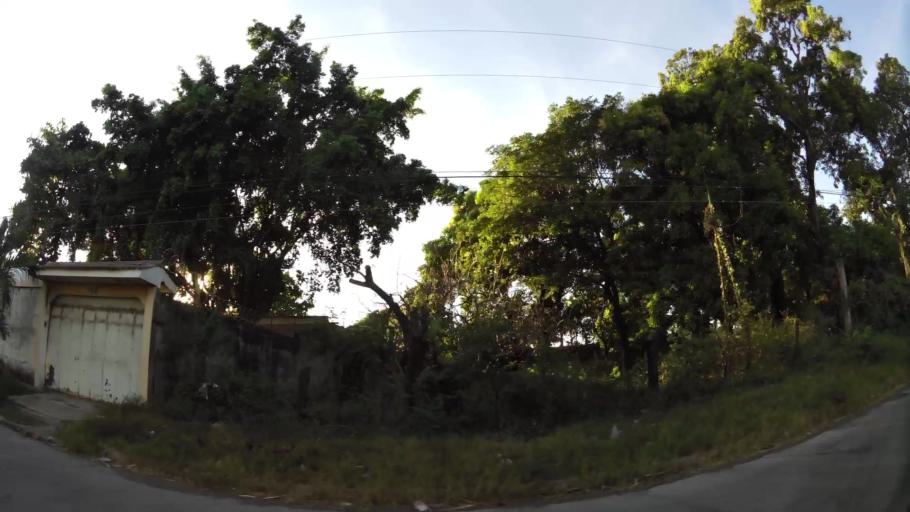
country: SV
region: San Miguel
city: San Miguel
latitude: 13.4590
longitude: -88.1767
